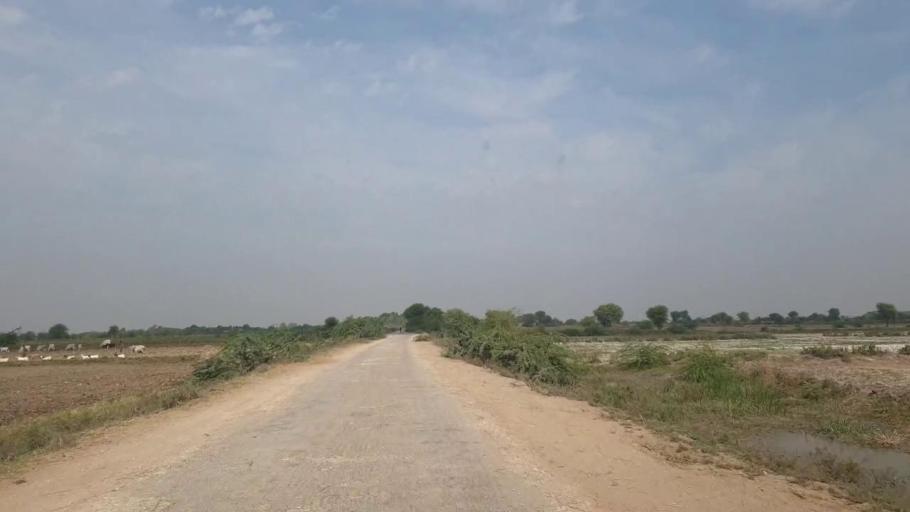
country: PK
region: Sindh
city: Rajo Khanani
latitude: 24.9332
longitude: 68.9877
